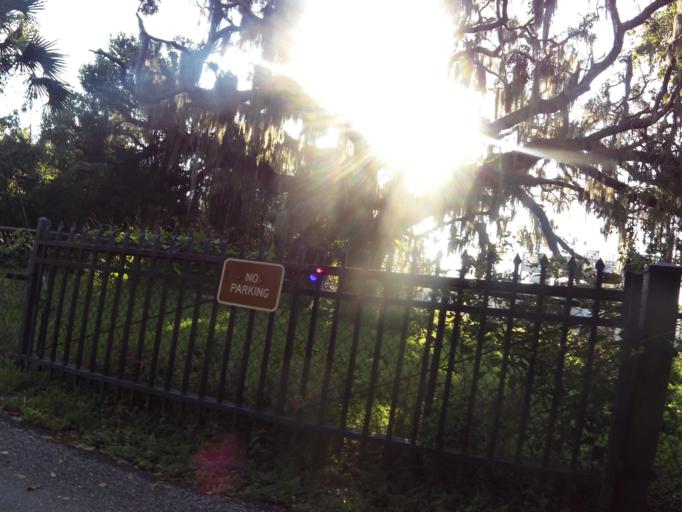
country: US
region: Florida
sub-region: Putnam County
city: Palatka
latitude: 29.6378
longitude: -81.6468
